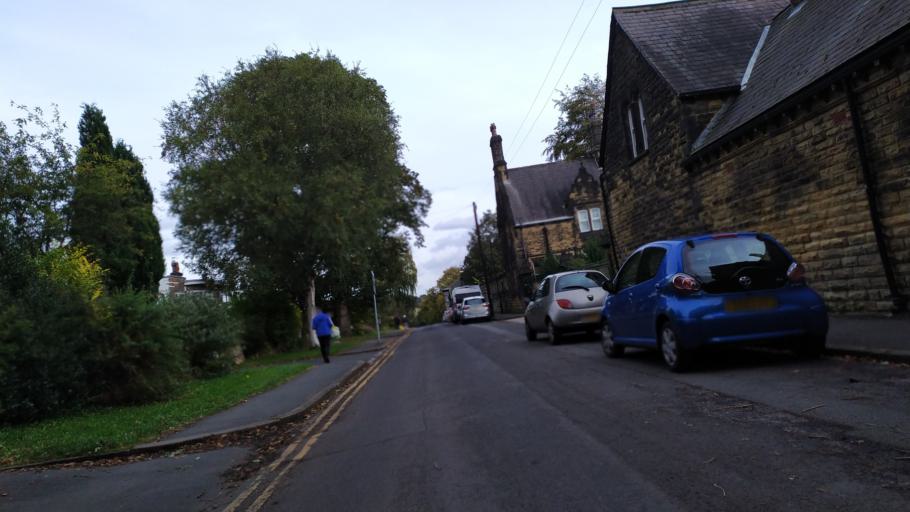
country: GB
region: England
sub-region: City and Borough of Leeds
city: Chapel Allerton
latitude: 53.8230
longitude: -1.5757
